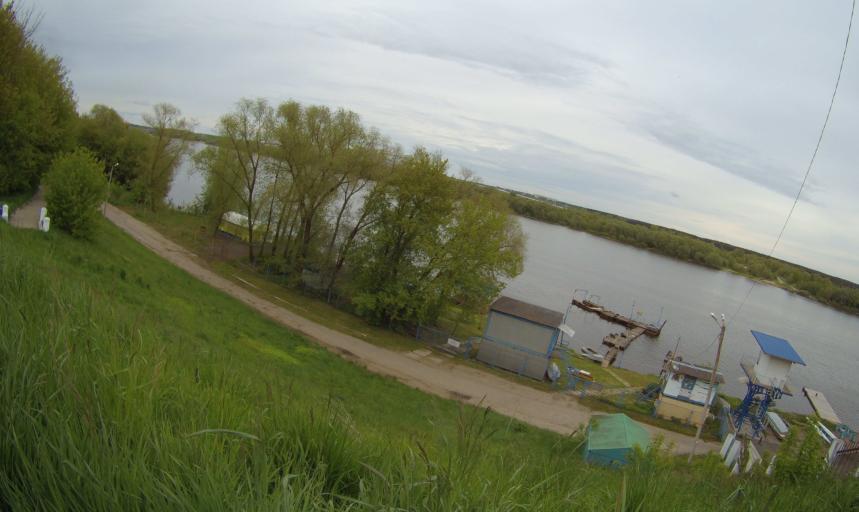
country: RU
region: Moskovskaya
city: Kolomna
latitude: 55.0700
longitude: 38.8052
